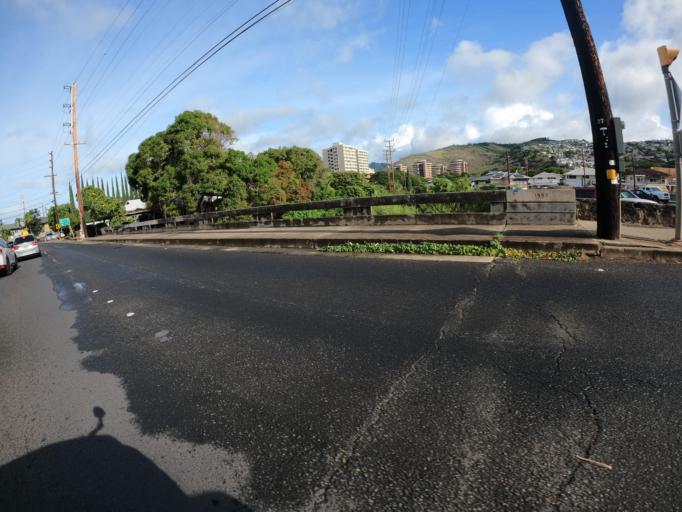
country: US
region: Hawaii
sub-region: Honolulu County
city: Honolulu
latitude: 21.2904
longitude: -157.8149
